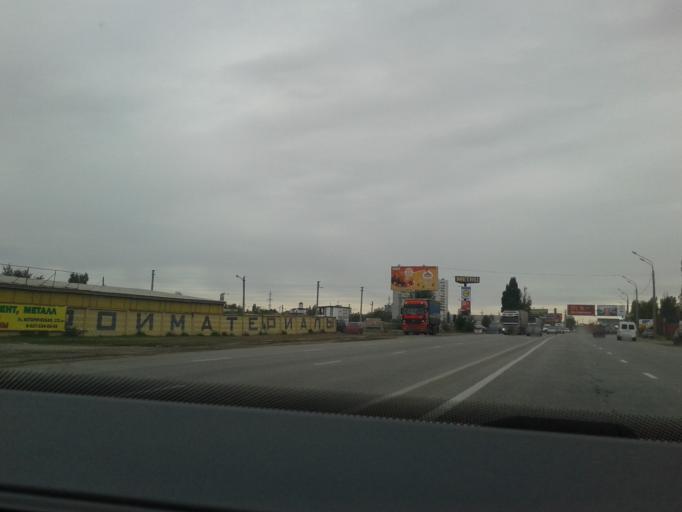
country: RU
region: Volgograd
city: Gorodishche
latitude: 48.7747
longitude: 44.4684
